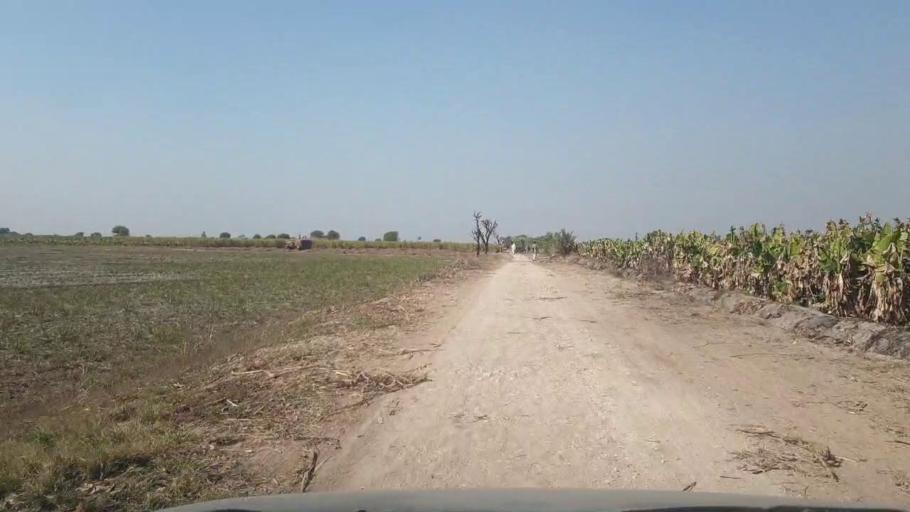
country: PK
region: Sindh
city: Chambar
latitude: 25.3260
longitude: 68.8670
